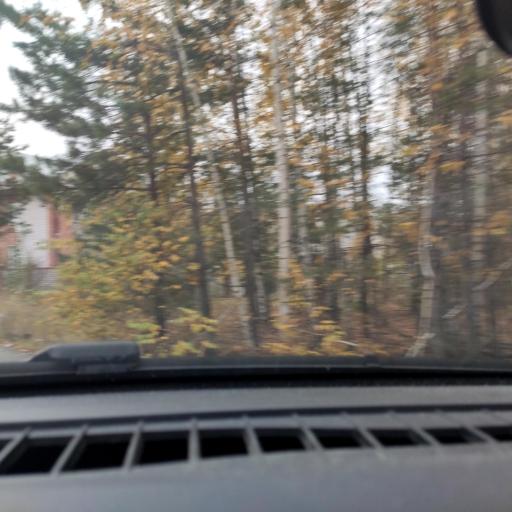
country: RU
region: Voronezj
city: Podgornoye
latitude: 51.7649
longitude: 39.1882
